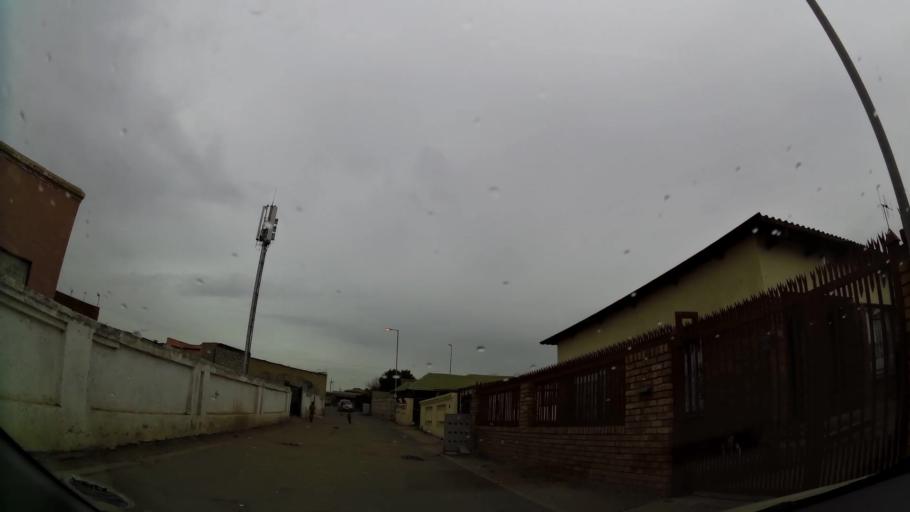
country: ZA
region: Gauteng
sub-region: City of Tshwane Metropolitan Municipality
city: Pretoria
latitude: -25.7103
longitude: 28.3518
